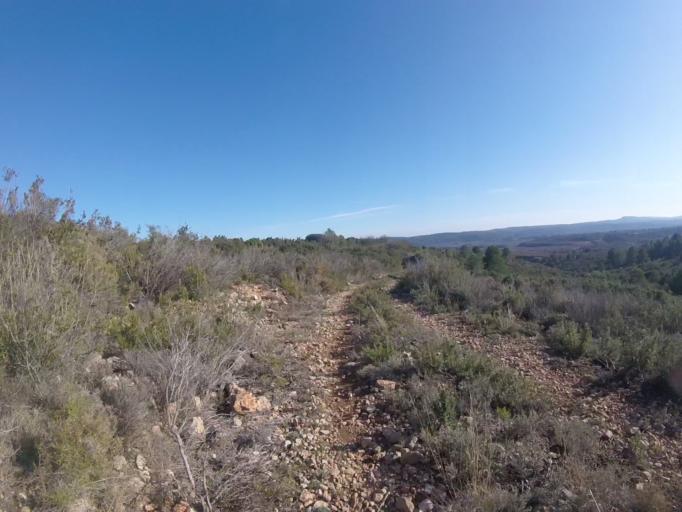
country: ES
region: Valencia
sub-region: Provincia de Castello
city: Sarratella
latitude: 40.2888
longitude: 0.0568
